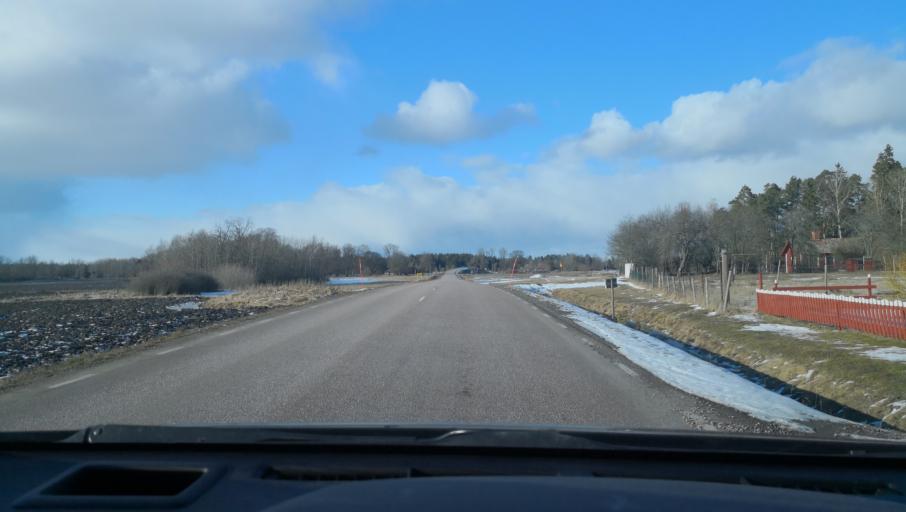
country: SE
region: Uppsala
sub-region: Enkopings Kommun
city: Hummelsta
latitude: 59.6382
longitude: 16.9699
